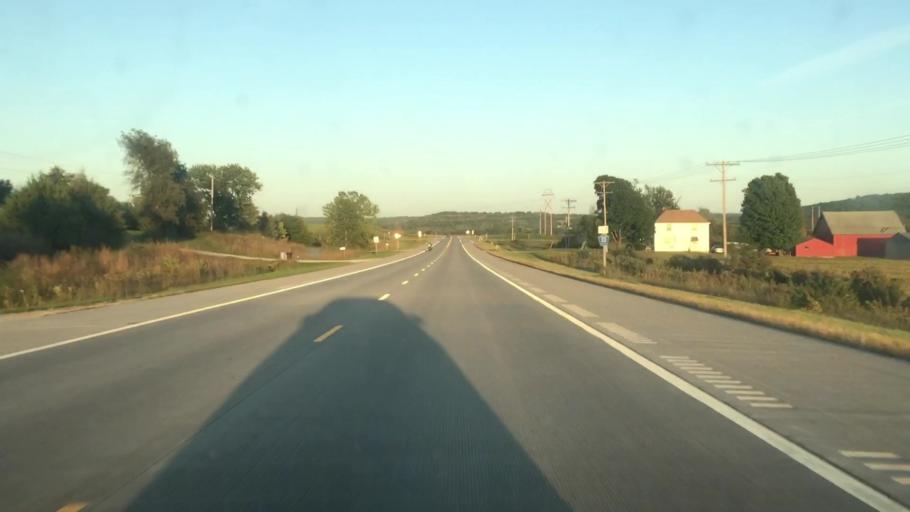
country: US
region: Kansas
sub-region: Leavenworth County
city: Leavenworth
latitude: 39.3534
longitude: -94.9966
